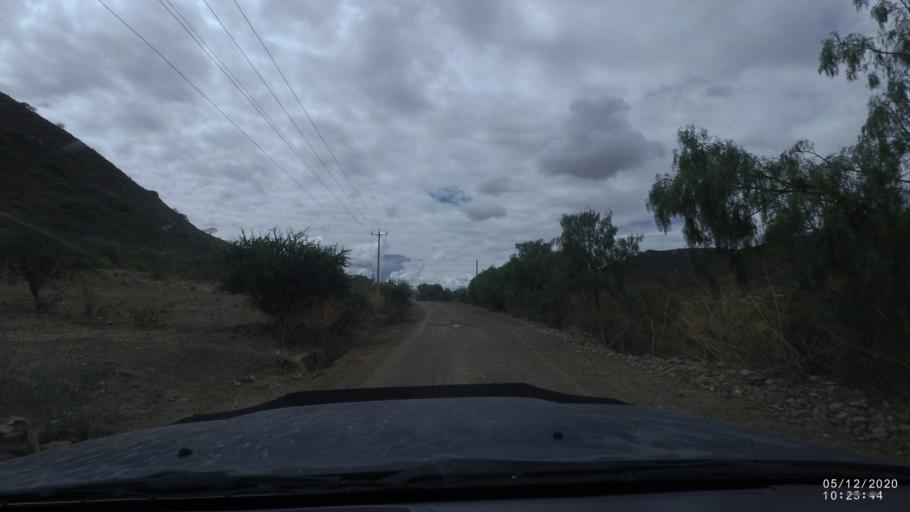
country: BO
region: Cochabamba
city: Sipe Sipe
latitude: -17.5204
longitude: -66.2867
